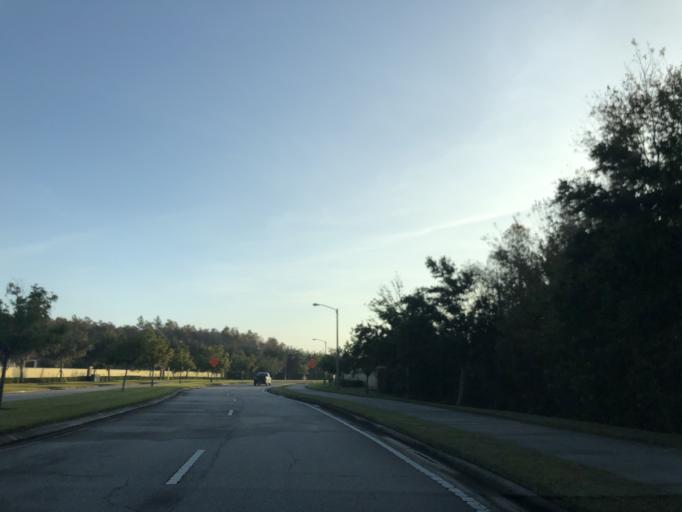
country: US
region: Florida
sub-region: Osceola County
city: Kissimmee
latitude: 28.3308
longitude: -81.4273
